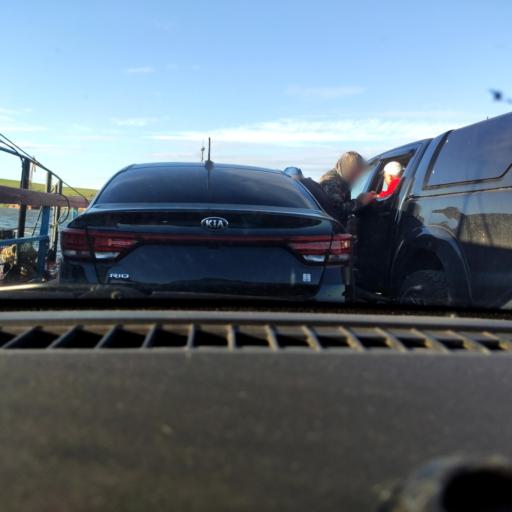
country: RU
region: Perm
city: Verkhnechusovskiye Gorodki
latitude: 58.1902
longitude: 57.1263
